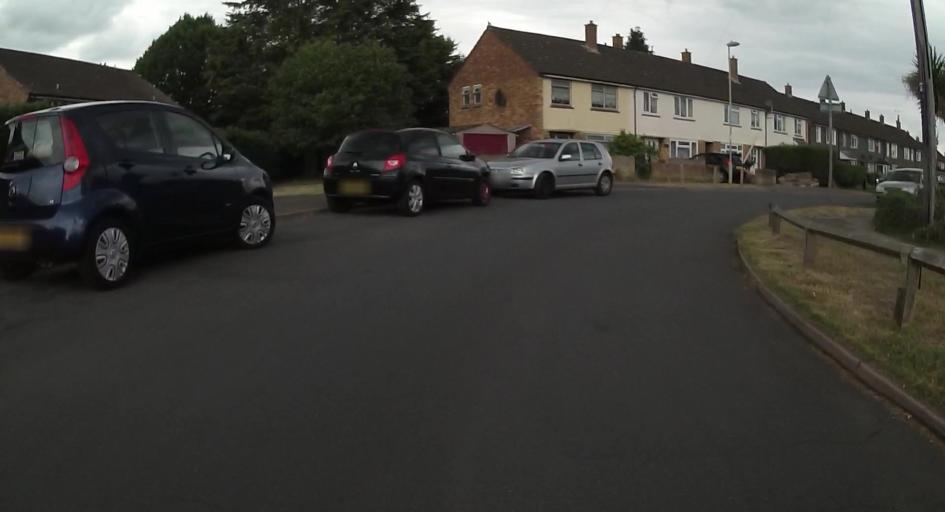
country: GB
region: England
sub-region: Surrey
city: Seale
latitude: 51.2377
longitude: -0.7408
